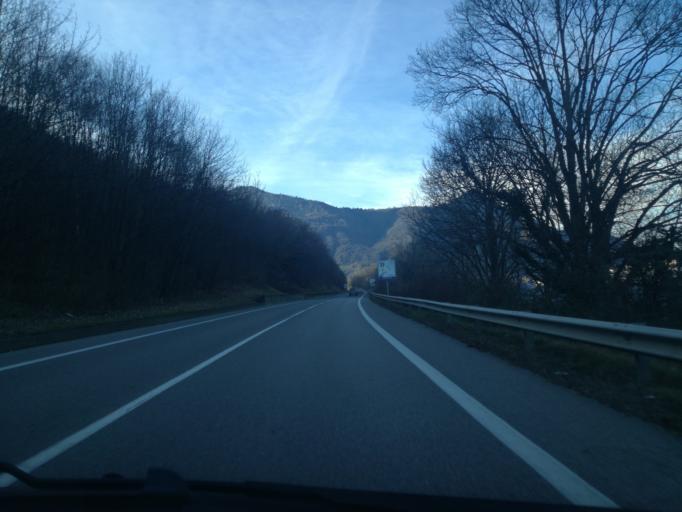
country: IT
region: Lombardy
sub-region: Provincia di Bergamo
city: Pianico
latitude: 45.8053
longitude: 10.0433
